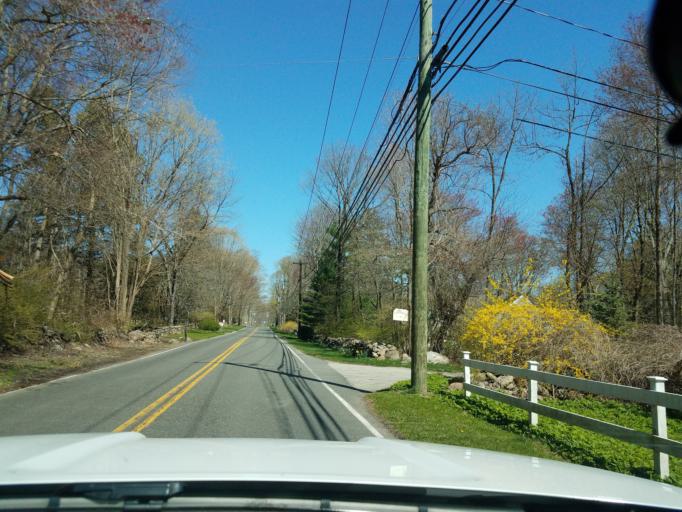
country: US
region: Connecticut
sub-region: Fairfield County
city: Westport
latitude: 41.2064
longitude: -73.3701
